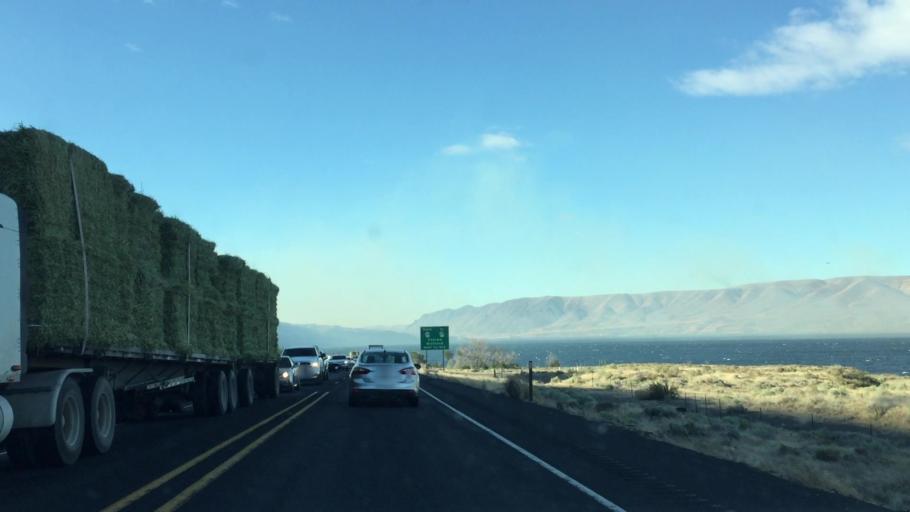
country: US
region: Washington
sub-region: Grant County
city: Mattawa
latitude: 46.9383
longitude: -119.9597
